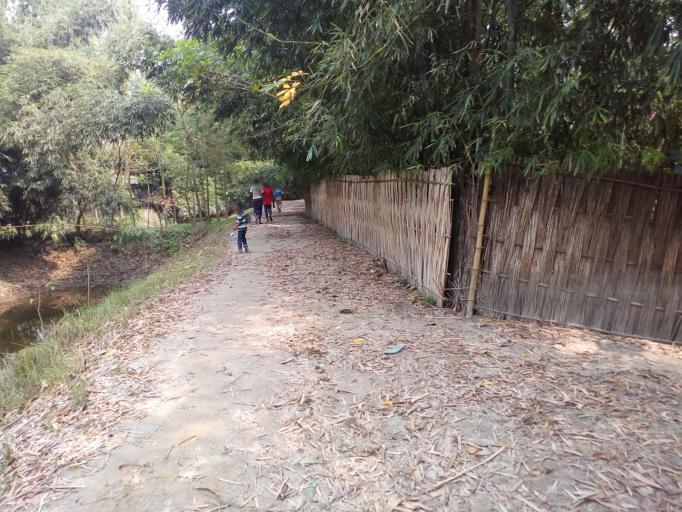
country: BD
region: Rangpur Division
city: Nageswari
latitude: 25.8906
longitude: 89.8187
